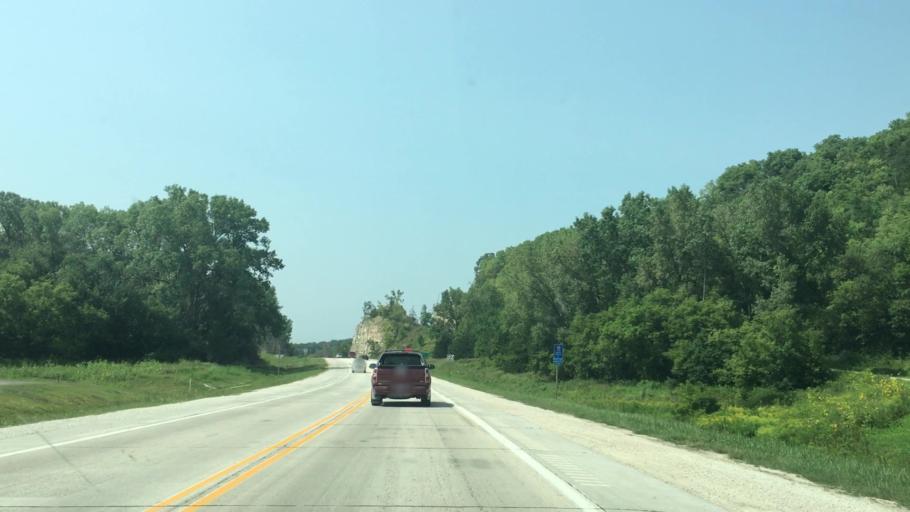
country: US
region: Iowa
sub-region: Winneshiek County
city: Decorah
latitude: 43.2927
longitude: -91.8059
